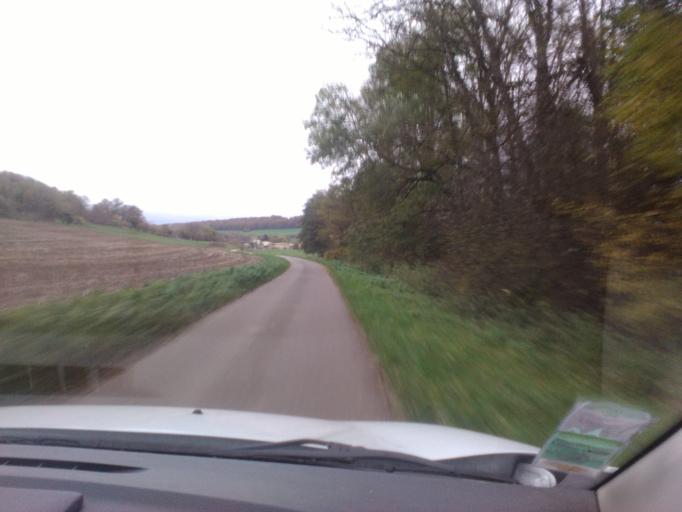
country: FR
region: Lorraine
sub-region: Departement des Vosges
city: Mirecourt
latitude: 48.2743
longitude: 6.2274
